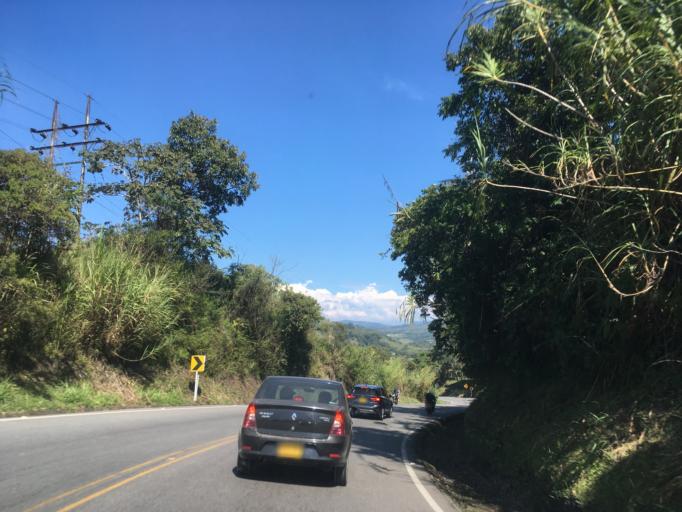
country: CO
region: Santander
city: Suaita
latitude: 6.0653
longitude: -73.4271
